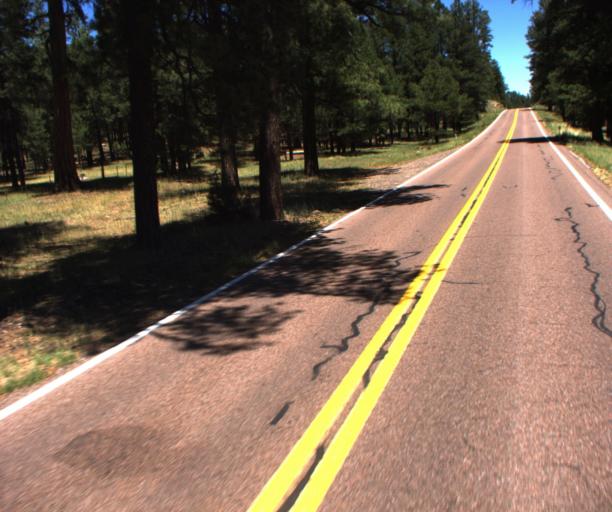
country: US
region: Arizona
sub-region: Gila County
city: Pine
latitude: 34.5411
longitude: -111.3267
